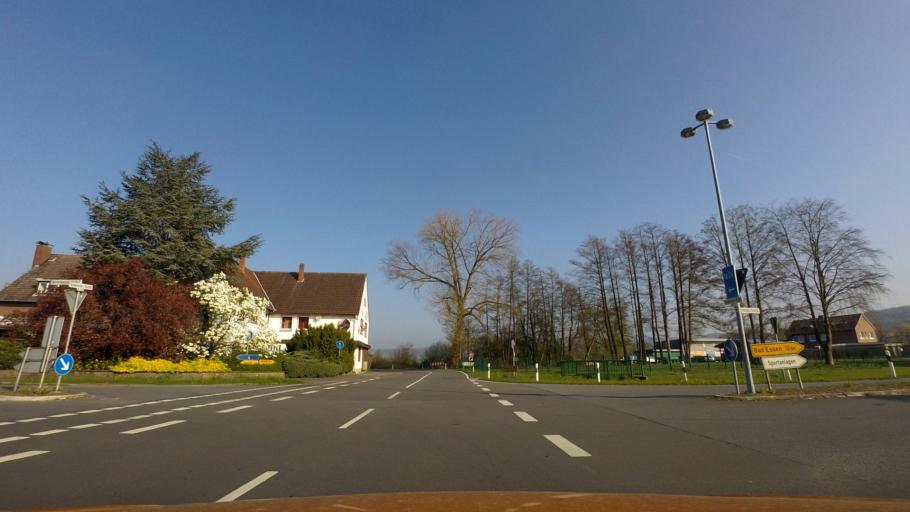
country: DE
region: Lower Saxony
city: Melle
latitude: 52.2411
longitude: 8.2865
